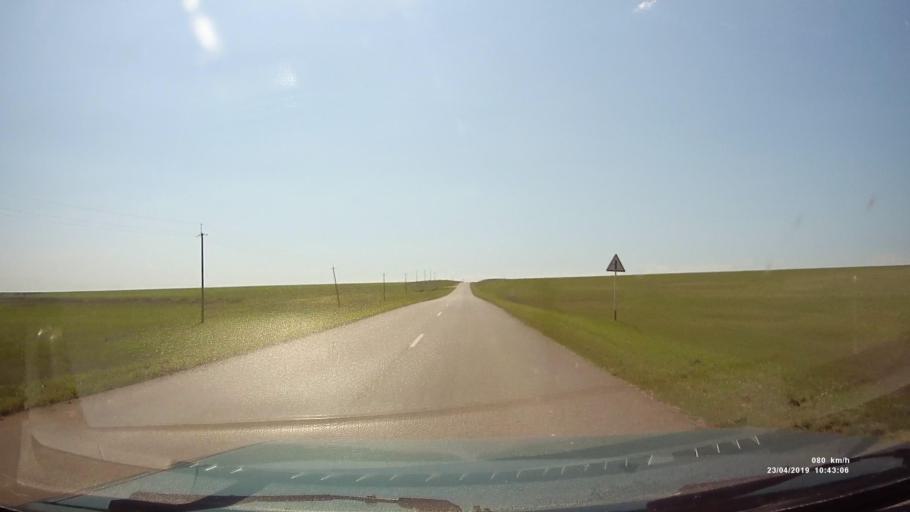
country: RU
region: Kalmykiya
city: Yashalta
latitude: 46.4741
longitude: 42.6484
